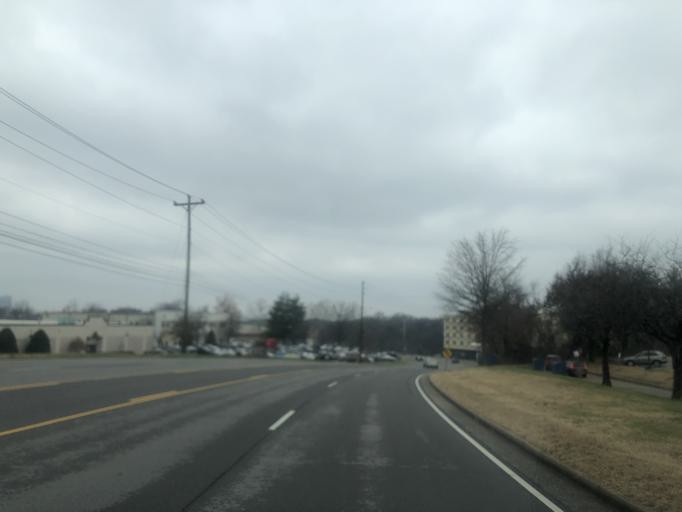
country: US
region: Tennessee
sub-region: Davidson County
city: Lakewood
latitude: 36.1485
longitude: -86.6741
